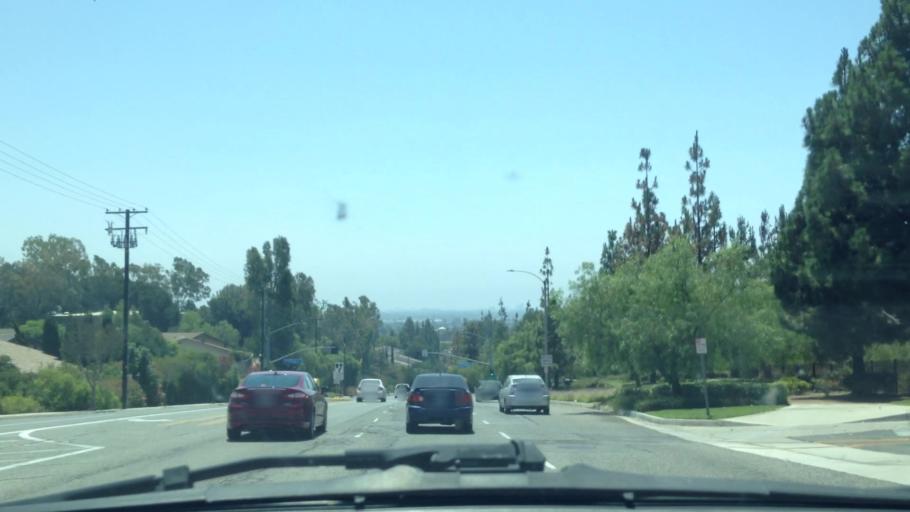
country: US
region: California
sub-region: Orange County
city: Brea
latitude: 33.8965
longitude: -117.8919
